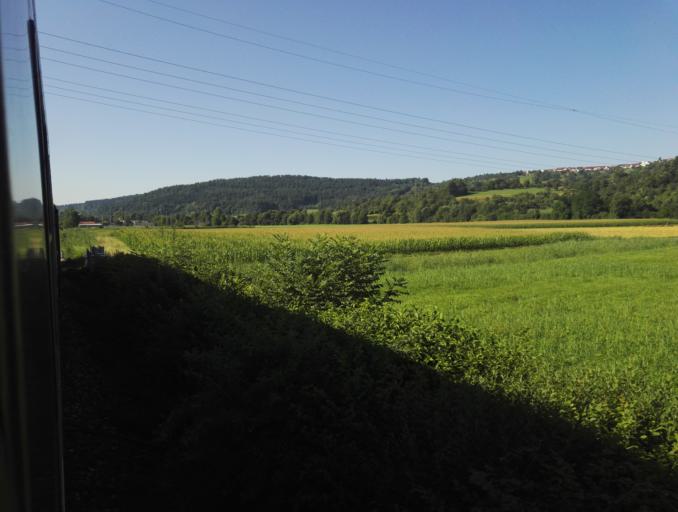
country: DE
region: Baden-Wuerttemberg
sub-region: Regierungsbezirk Stuttgart
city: Rudersberg
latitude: 48.8527
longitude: 9.5381
